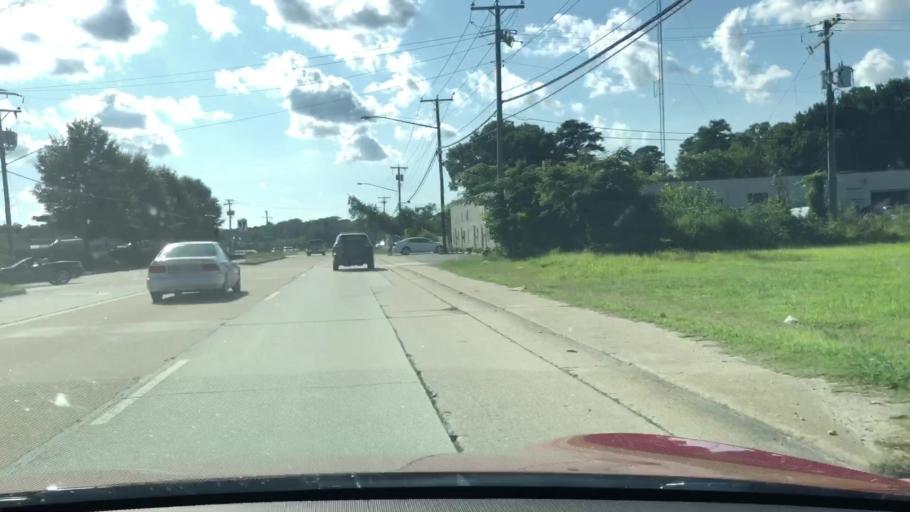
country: US
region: Virginia
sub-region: City of Virginia Beach
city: Virginia Beach
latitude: 36.8440
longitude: -76.0326
